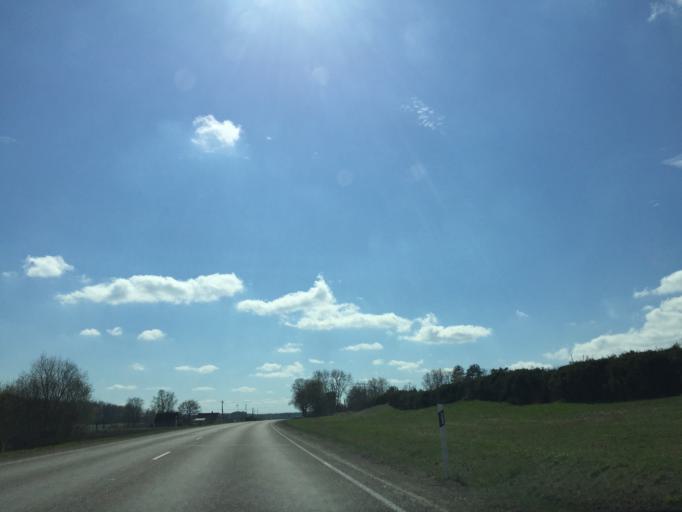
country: EE
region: Valgamaa
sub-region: Torva linn
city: Torva
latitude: 58.0384
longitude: 26.1843
